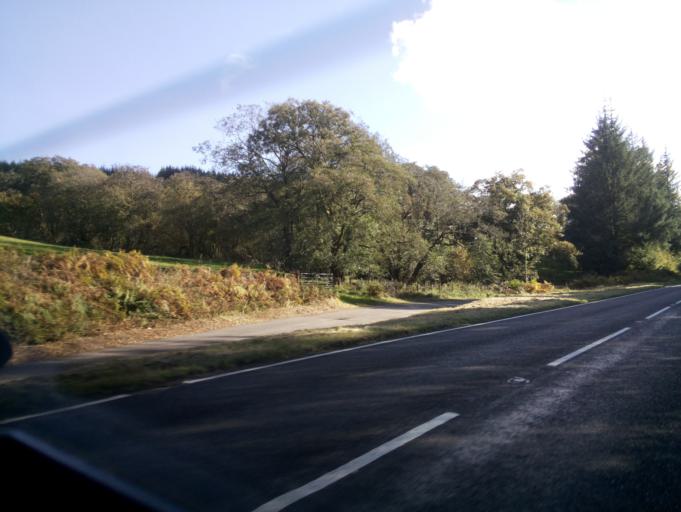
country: GB
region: Wales
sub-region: Merthyr Tydfil County Borough
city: Merthyr Tydfil
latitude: 51.8001
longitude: -3.4386
